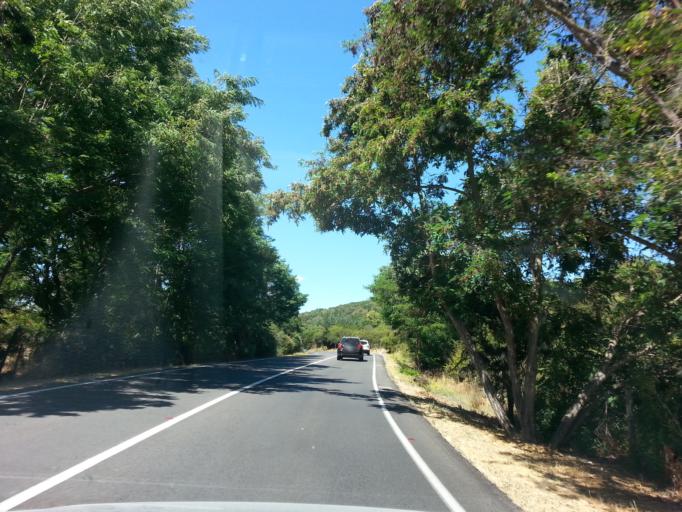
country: CL
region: Valparaiso
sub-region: Provincia de Marga Marga
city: Villa Alemana
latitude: -33.2039
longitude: -71.3819
